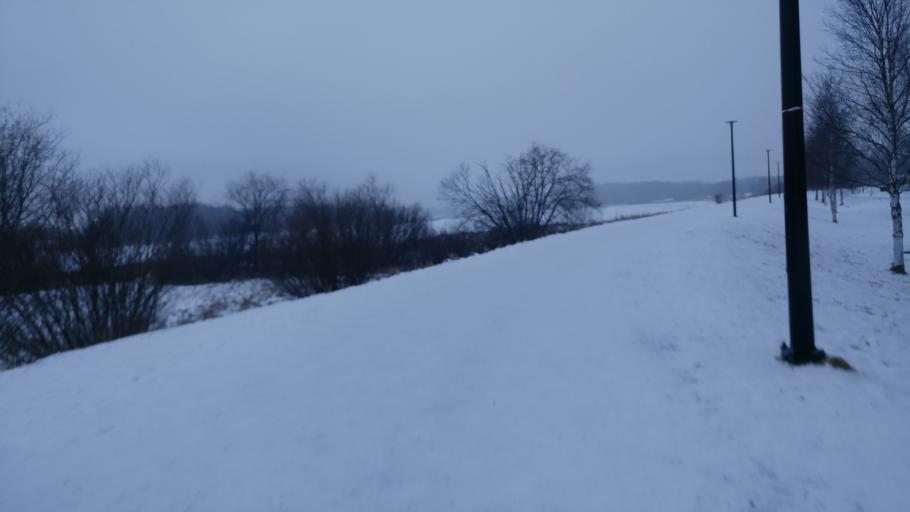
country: NO
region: Akershus
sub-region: Skedsmo
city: Lillestrom
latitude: 59.9601
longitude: 11.0293
